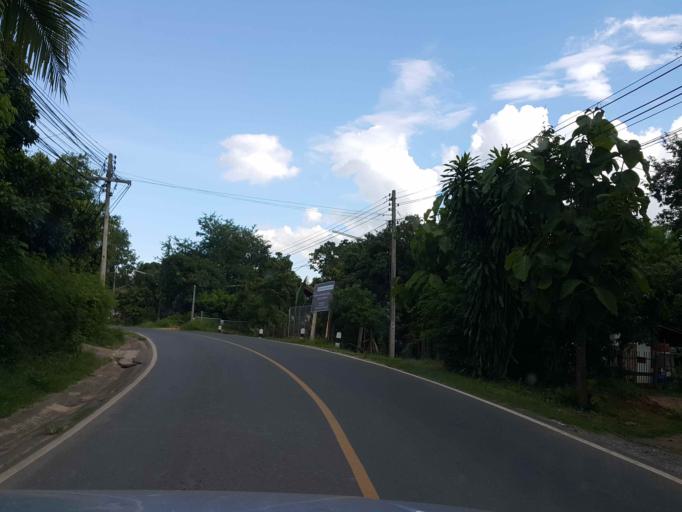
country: TH
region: Chiang Mai
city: Mae Taeng
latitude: 18.9713
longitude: 98.9200
